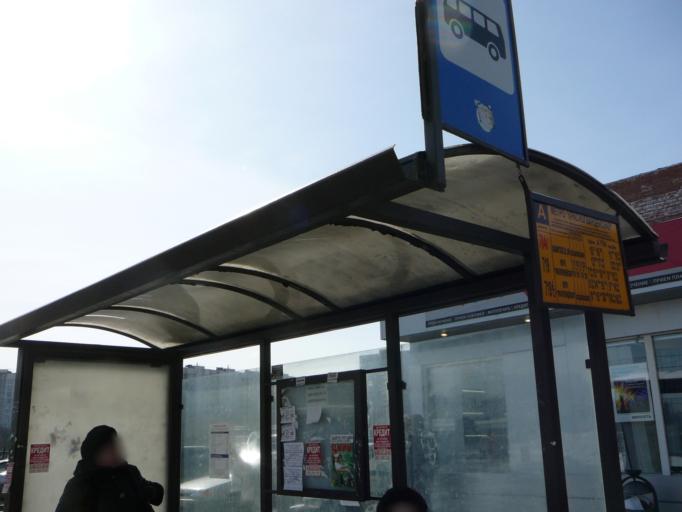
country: RU
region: Moscow
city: Orekhovo-Borisovo
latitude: 55.6130
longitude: 37.7444
